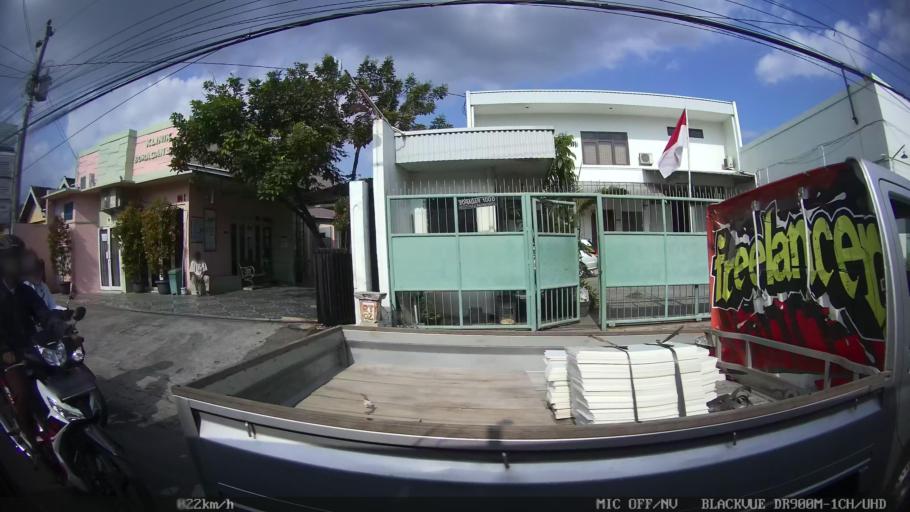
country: ID
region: Daerah Istimewa Yogyakarta
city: Yogyakarta
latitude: -7.7929
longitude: 110.3473
